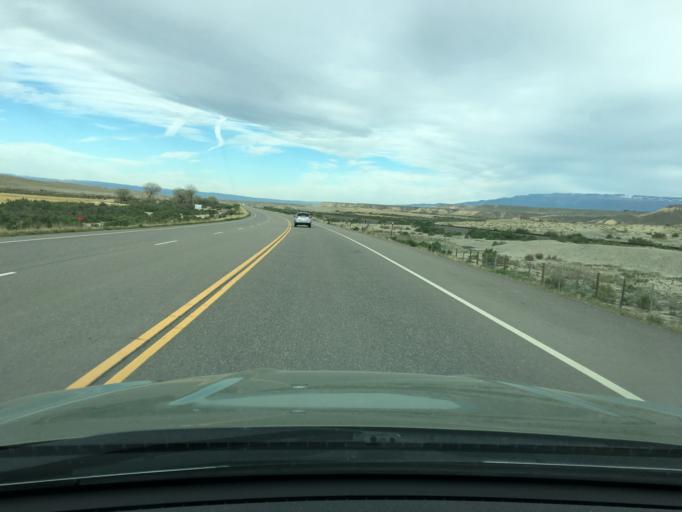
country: US
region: Colorado
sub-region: Delta County
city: Orchard City
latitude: 38.8029
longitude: -107.8813
